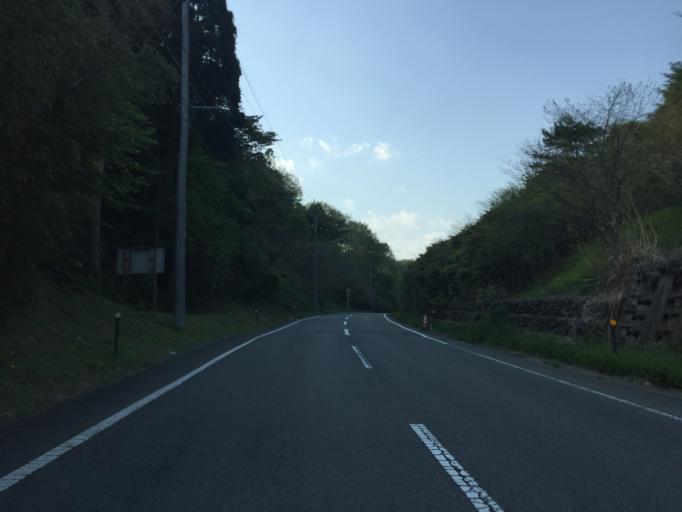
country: JP
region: Fukushima
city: Iwaki
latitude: 36.9695
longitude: 140.8387
